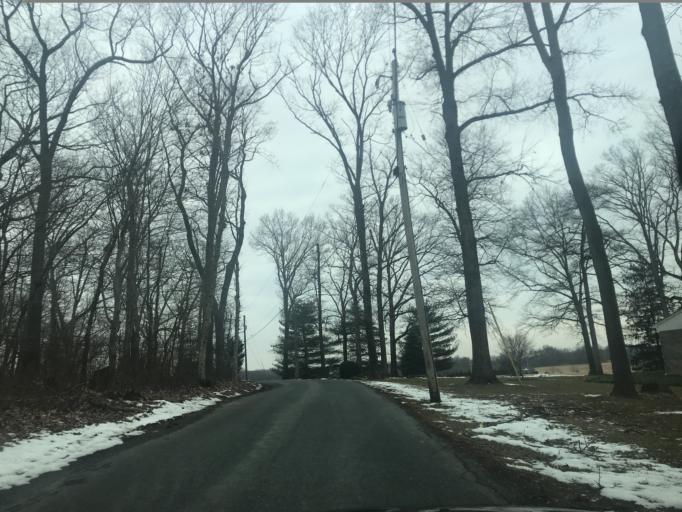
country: US
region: Pennsylvania
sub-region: York County
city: Stewartstown
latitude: 39.6945
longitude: -76.5280
